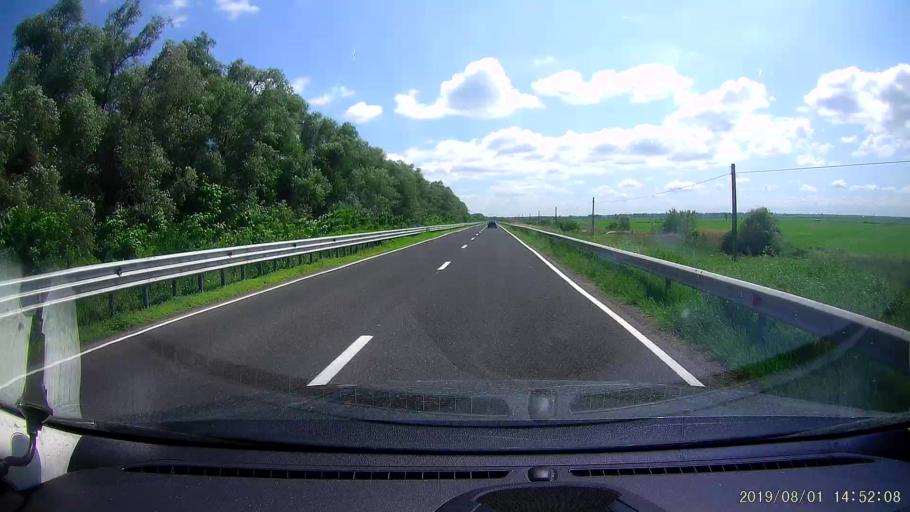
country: RO
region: Braila
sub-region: Comuna Vadeni
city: Vadeni
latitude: 45.3616
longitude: 28.0128
